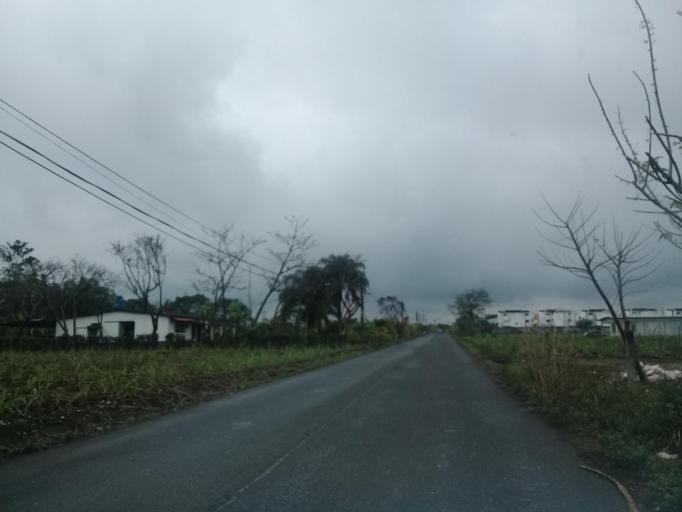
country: MX
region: Veracruz
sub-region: Cordoba
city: San Jose de Tapia
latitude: 18.8333
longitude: -96.9561
